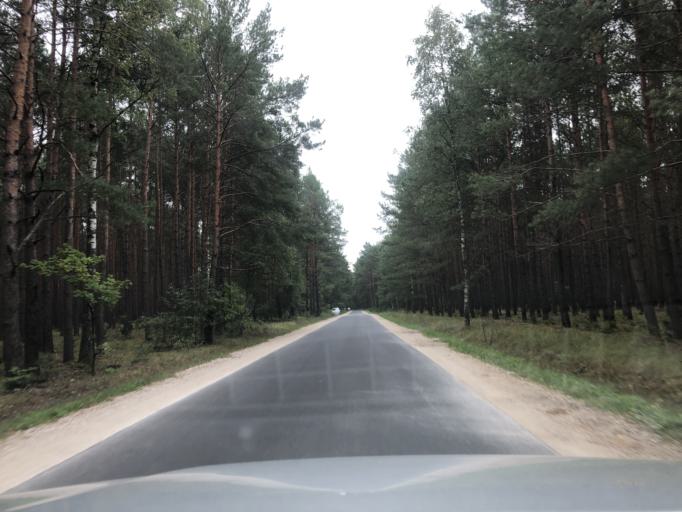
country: PL
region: Greater Poland Voivodeship
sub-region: Powiat pilski
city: Pila
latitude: 53.2558
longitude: 16.7005
